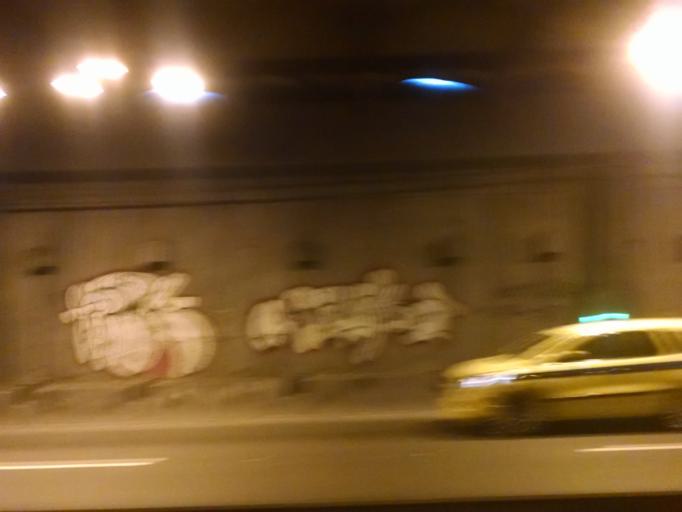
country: BR
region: Rio de Janeiro
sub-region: Rio De Janeiro
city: Rio de Janeiro
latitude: -22.9817
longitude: -43.2338
